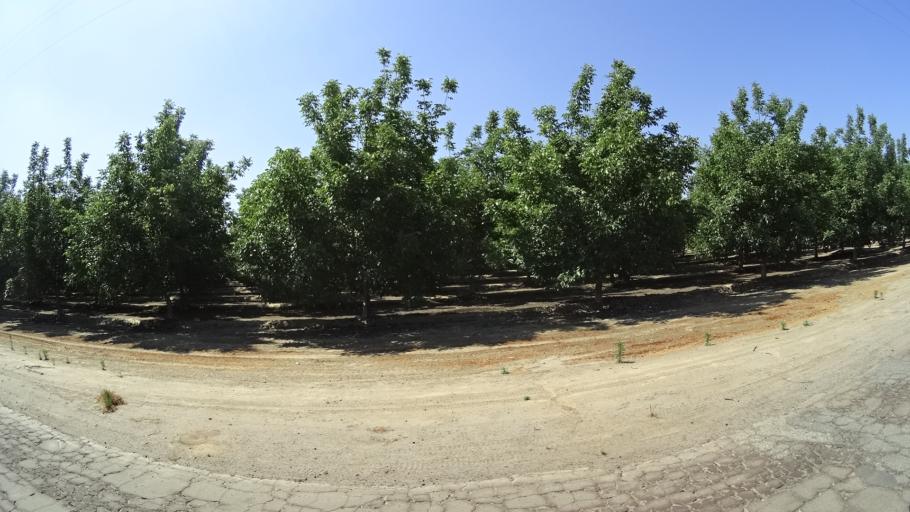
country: US
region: California
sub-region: Fresno County
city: Kingsburg
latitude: 36.4741
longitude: -119.5682
